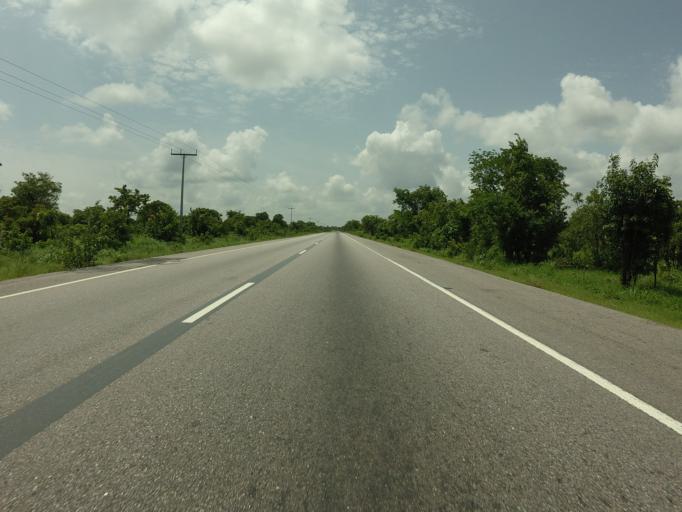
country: GH
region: Northern
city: Tamale
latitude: 9.1290
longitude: -1.2284
